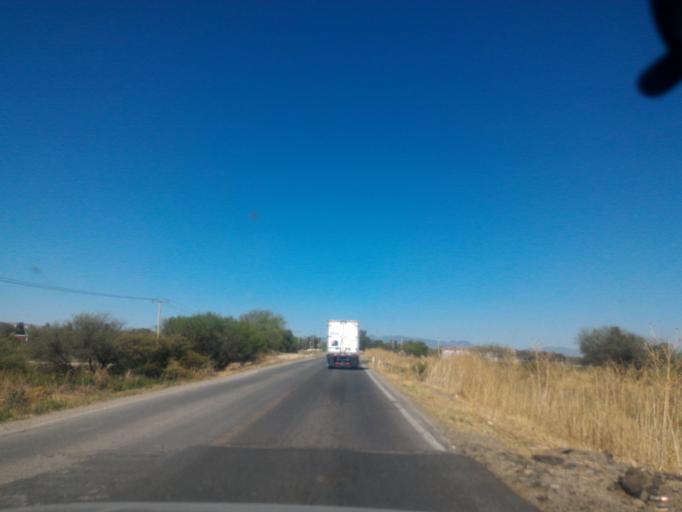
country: MX
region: Guanajuato
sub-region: San Francisco del Rincon
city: San Roque de Montes
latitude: 21.0273
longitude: -101.7827
